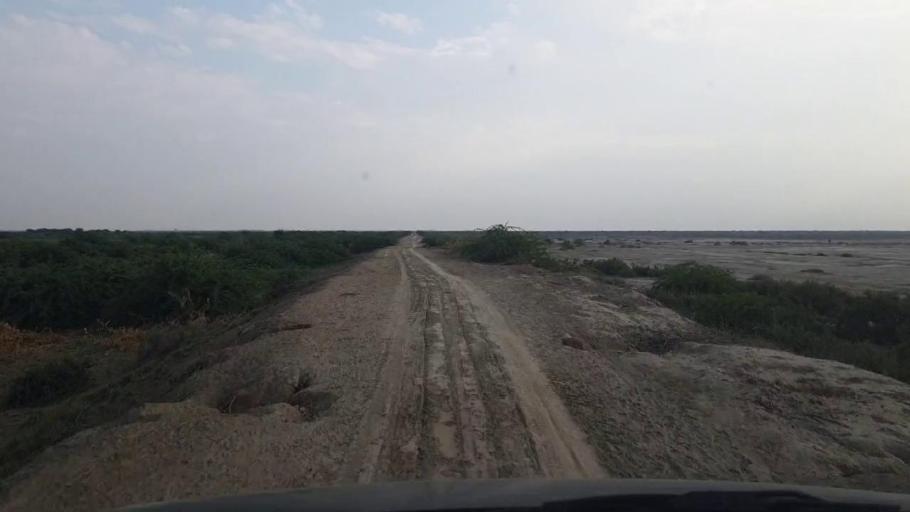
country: PK
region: Sindh
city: Badin
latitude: 24.4826
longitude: 68.6979
